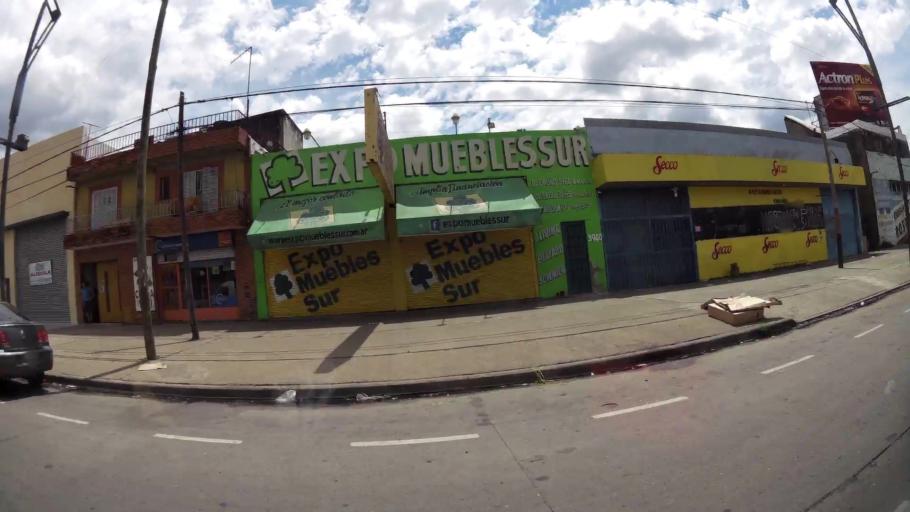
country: AR
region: Santa Fe
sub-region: Departamento de Rosario
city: Rosario
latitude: -32.9804
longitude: -60.6628
